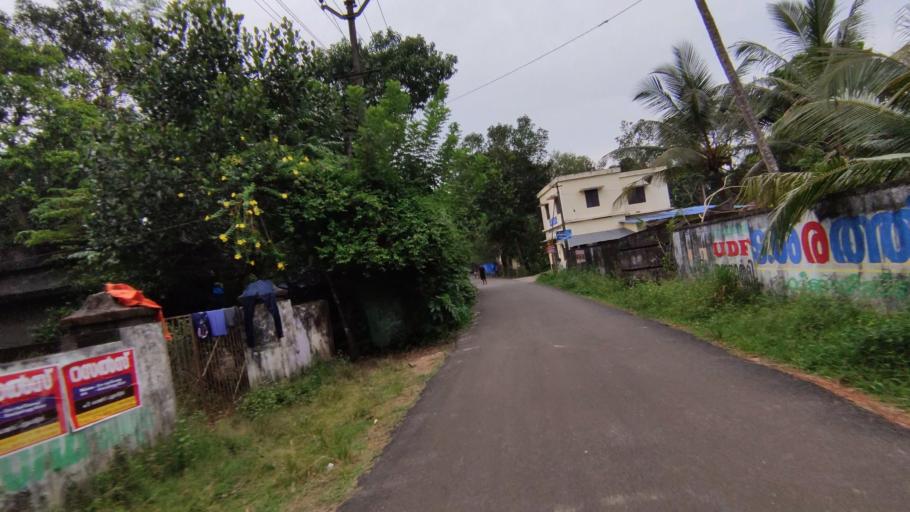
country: IN
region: Kerala
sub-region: Alappuzha
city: Shertallai
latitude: 9.6331
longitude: 76.3592
